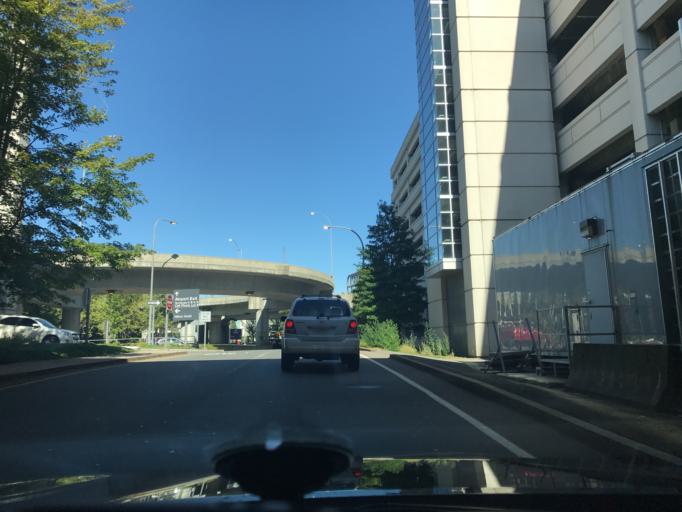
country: US
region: Massachusetts
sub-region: Suffolk County
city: Chelsea
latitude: 42.3667
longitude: -71.0199
